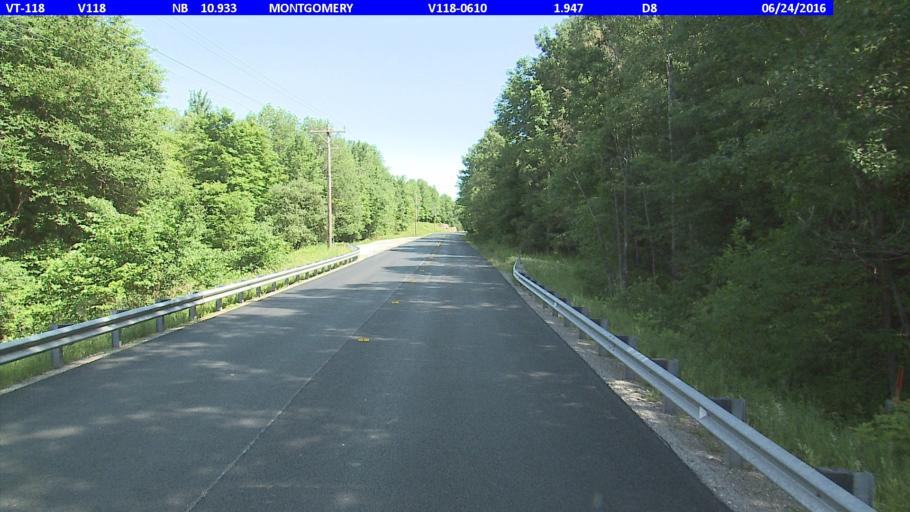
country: US
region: Vermont
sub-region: Franklin County
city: Richford
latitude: 44.8260
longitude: -72.6096
